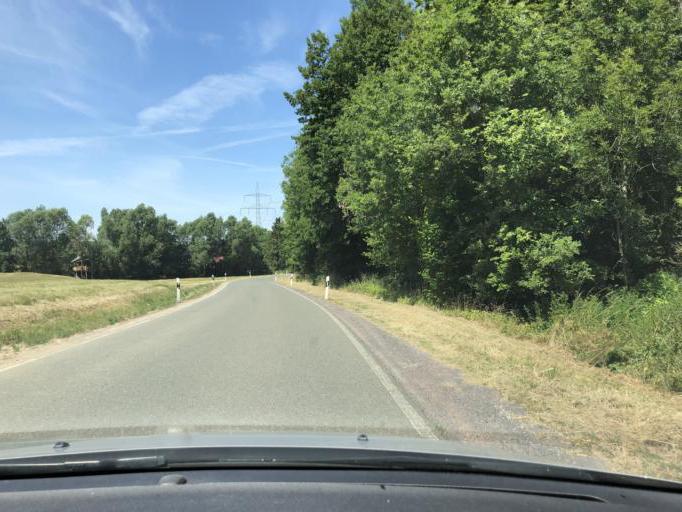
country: DE
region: Thuringia
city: Camburg
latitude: 51.0618
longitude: 11.7275
